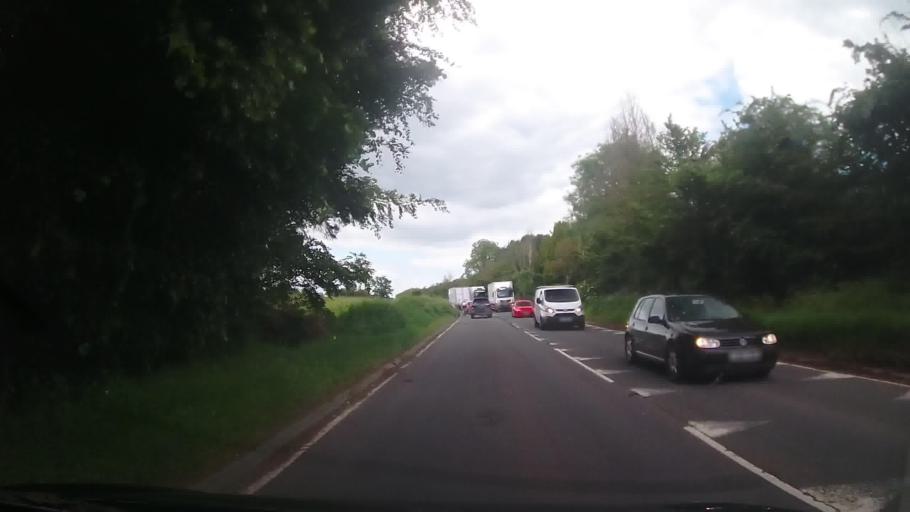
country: GB
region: England
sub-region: Herefordshire
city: Hereford
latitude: 52.0780
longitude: -2.7225
